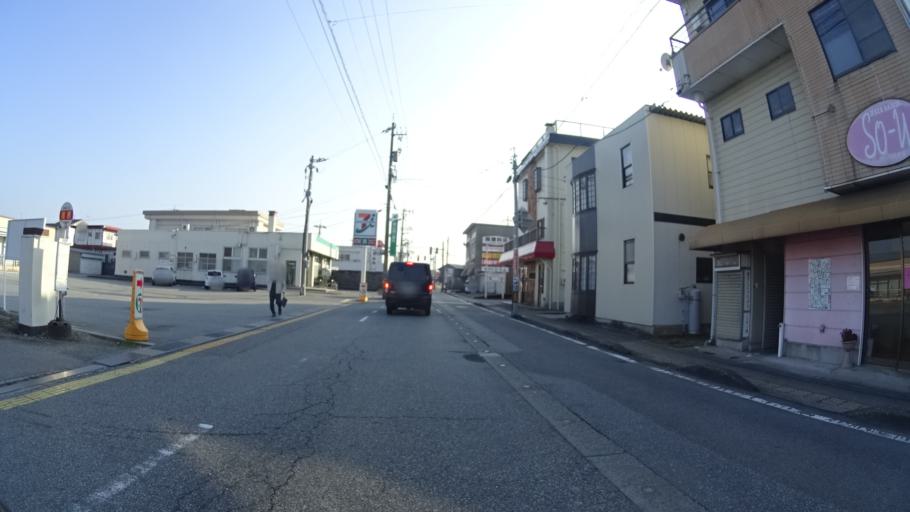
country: JP
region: Toyama
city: Toyama-shi
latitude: 36.6985
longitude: 137.2648
